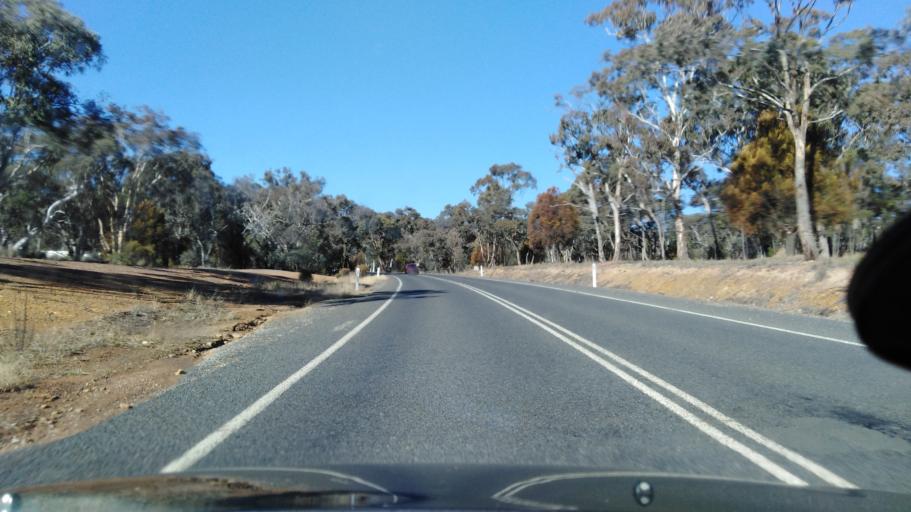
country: AU
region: New South Wales
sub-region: Yass Valley
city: Gundaroo
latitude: -35.1839
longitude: 149.2953
